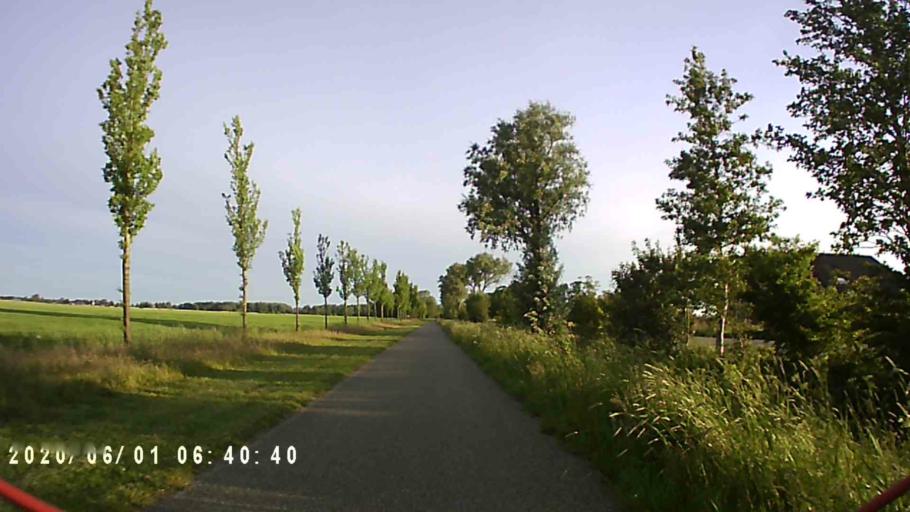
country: NL
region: Friesland
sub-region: Gemeente Kollumerland en Nieuwkruisland
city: Kollum
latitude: 53.2933
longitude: 6.1566
